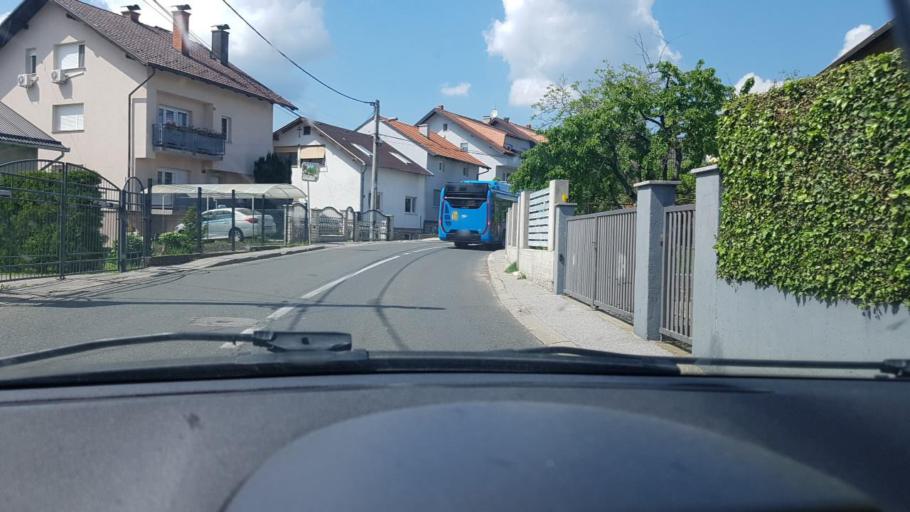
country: HR
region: Grad Zagreb
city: Zagreb
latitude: 45.8399
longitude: 16.0077
